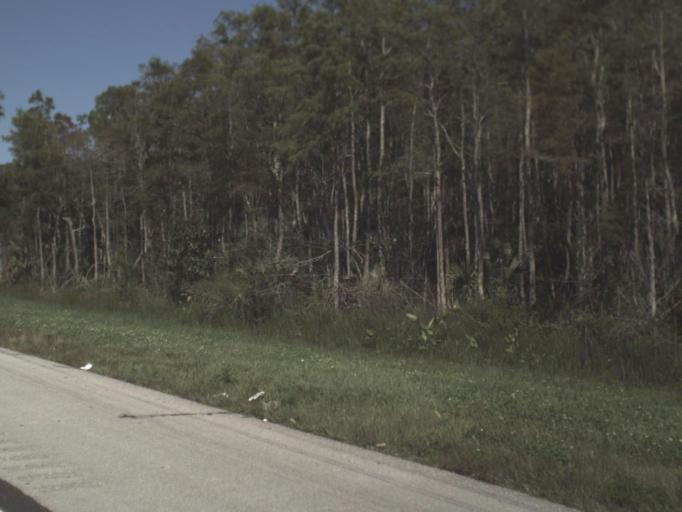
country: US
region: Florida
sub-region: Lee County
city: Bonita Springs
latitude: 26.3132
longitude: -81.7446
